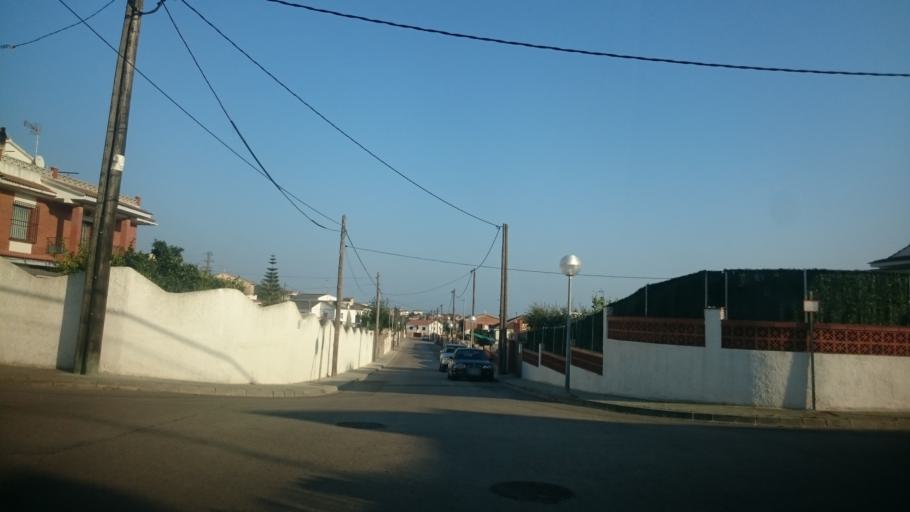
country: ES
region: Catalonia
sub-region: Provincia de Barcelona
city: Cubelles
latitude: 41.2223
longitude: 1.6705
